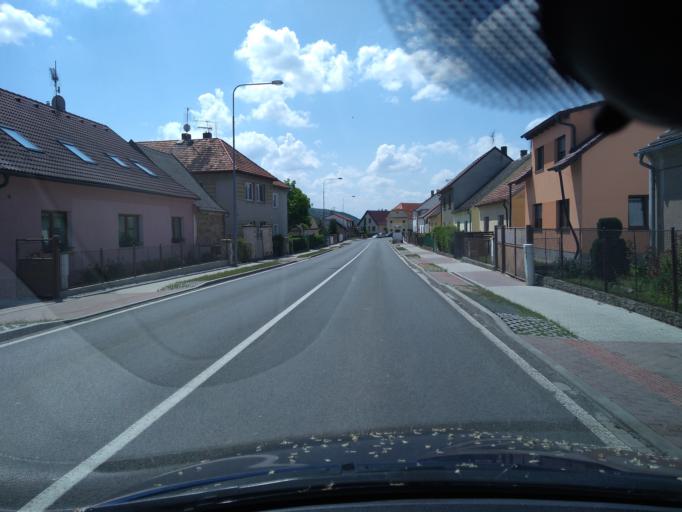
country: CZ
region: Plzensky
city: Prestice
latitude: 49.5452
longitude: 13.3150
